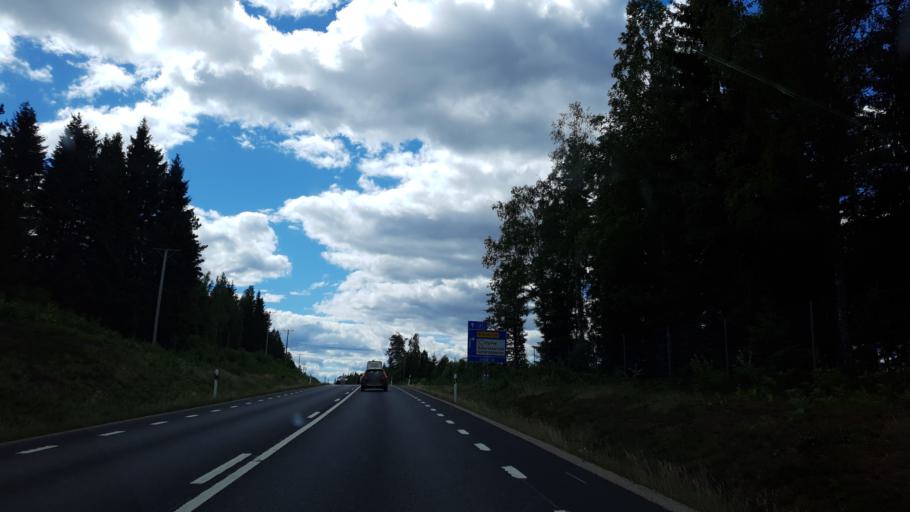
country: SE
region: Kronoberg
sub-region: Vaxjo Kommun
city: Braas
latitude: 57.1832
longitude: 15.1571
